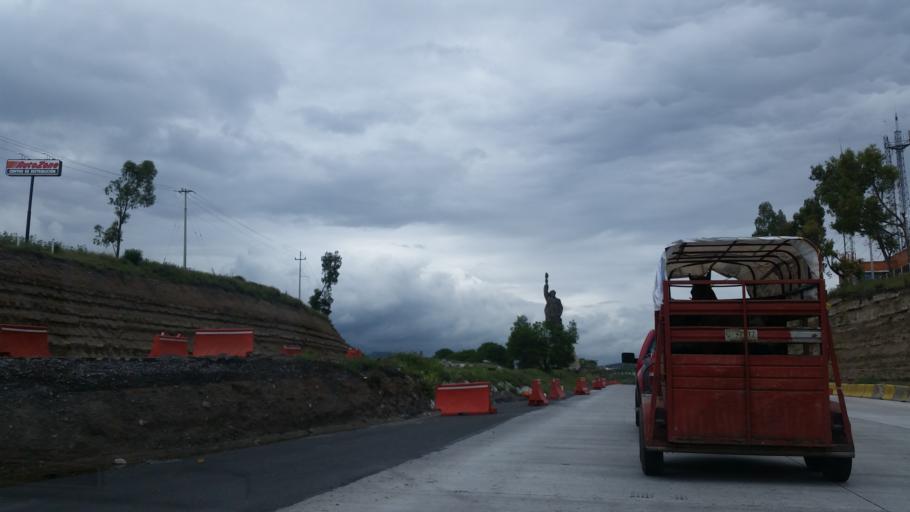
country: MX
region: Hidalgo
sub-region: Tepeji del Rio de Ocampo
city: Cantera de Villagran
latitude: 19.8534
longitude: -99.2885
